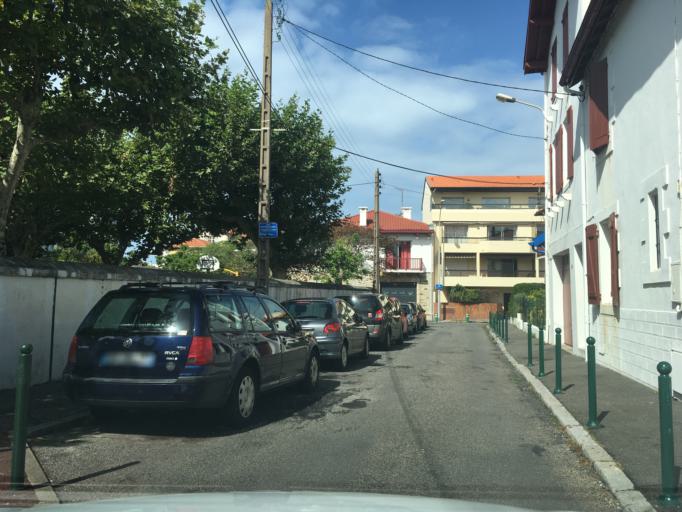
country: FR
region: Aquitaine
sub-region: Departement des Pyrenees-Atlantiques
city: Biarritz
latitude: 43.4772
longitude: -1.5635
